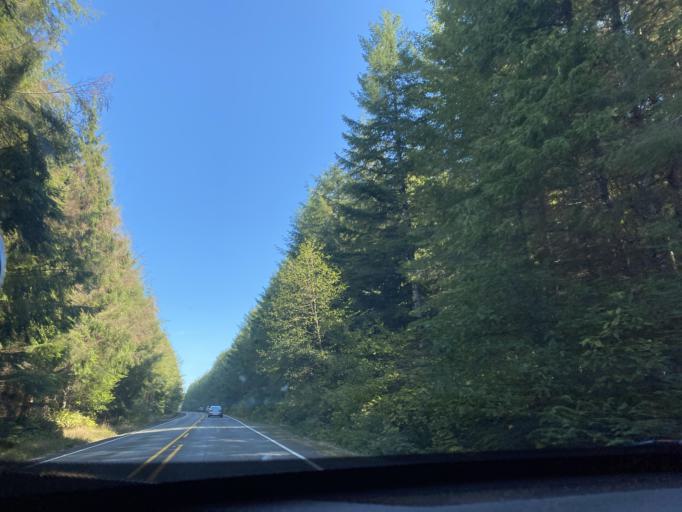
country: US
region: Washington
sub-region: Clallam County
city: Forks
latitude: 47.9201
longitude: -124.5125
